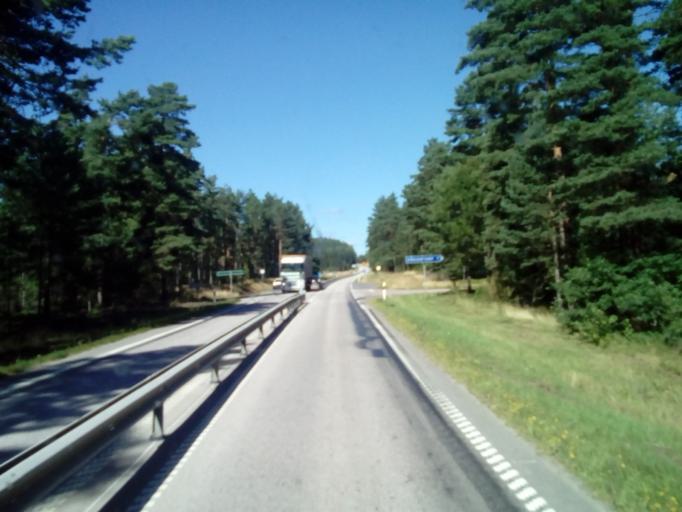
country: SE
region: OEstergoetland
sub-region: Kinda Kommun
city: Rimforsa
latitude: 58.0731
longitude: 15.6540
